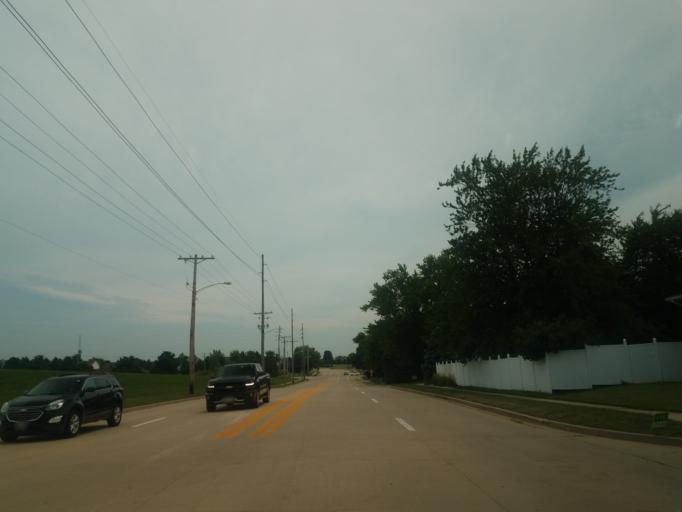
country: US
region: Illinois
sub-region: McLean County
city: Normal
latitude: 40.5199
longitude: -88.9437
